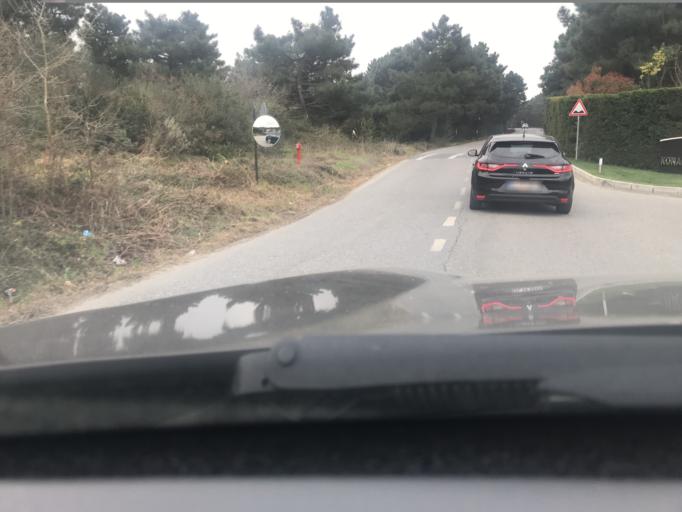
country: TR
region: Istanbul
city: Umraniye
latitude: 41.0443
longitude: 29.1703
